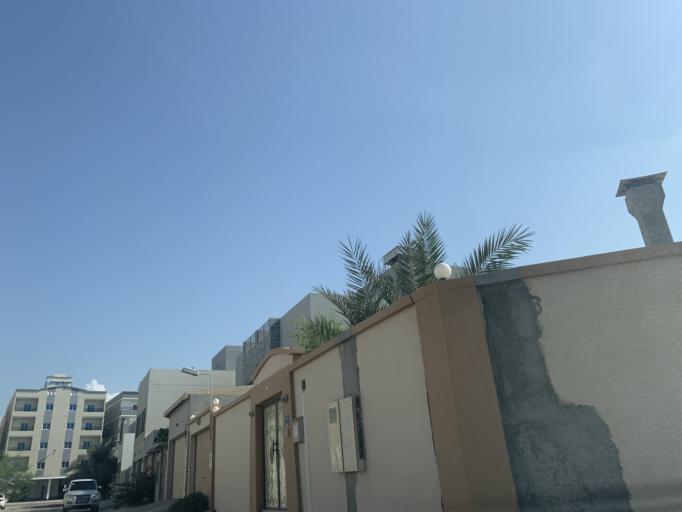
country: BH
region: Central Governorate
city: Madinat Hamad
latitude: 26.1342
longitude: 50.4870
